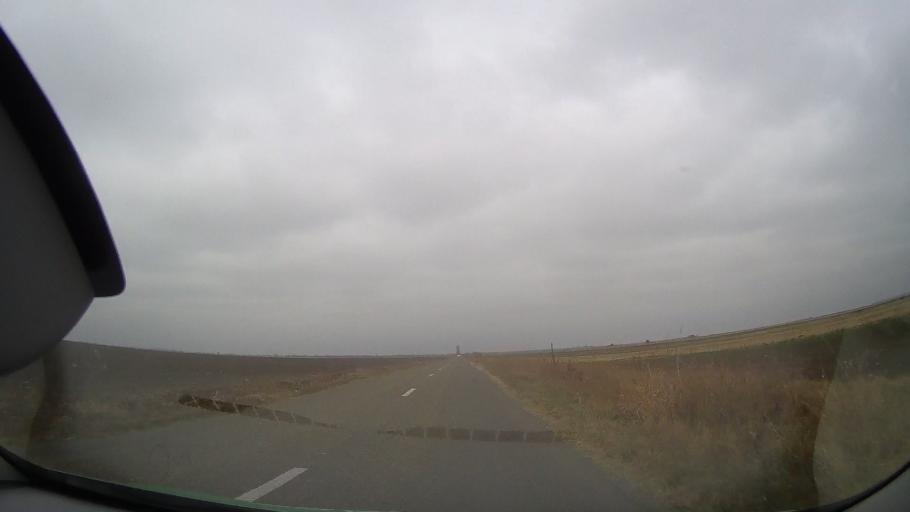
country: RO
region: Buzau
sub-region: Comuna Bradeanu
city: Bradeanu
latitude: 44.8968
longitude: 26.8729
